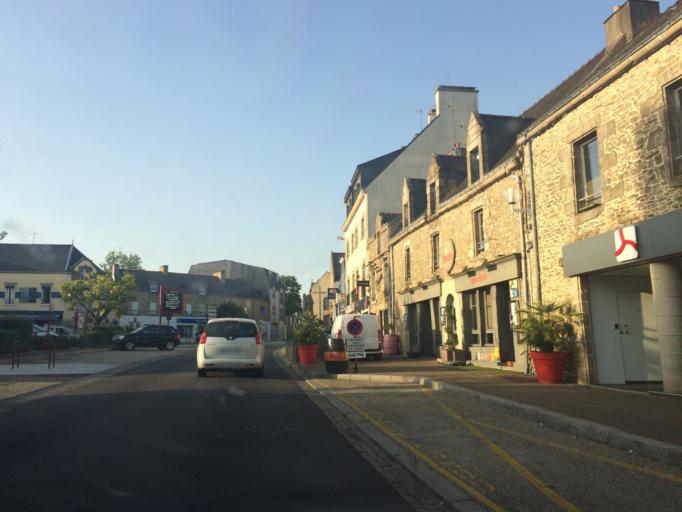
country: FR
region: Brittany
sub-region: Departement du Morbihan
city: Muzillac
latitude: 47.5530
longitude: -2.4822
